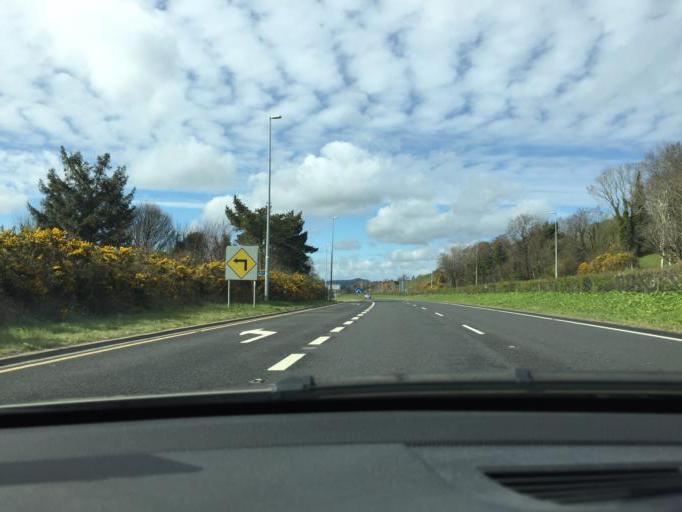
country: IE
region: Leinster
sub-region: Wicklow
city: Kilmacanoge
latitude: 53.1529
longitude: -6.1250
